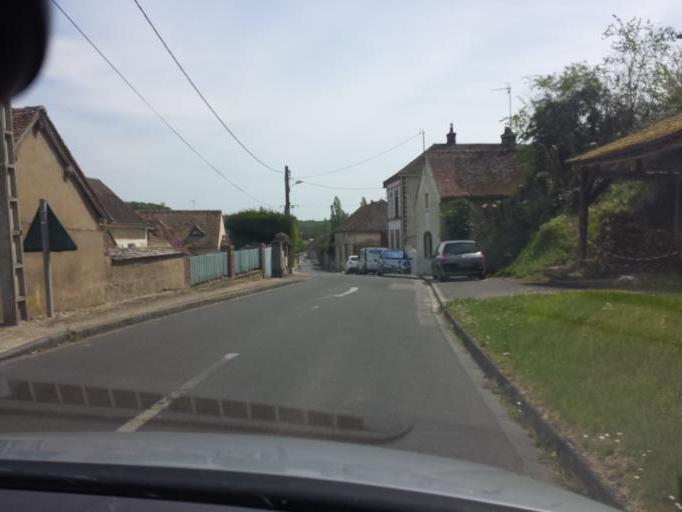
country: FR
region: Centre
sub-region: Departement d'Eure-et-Loir
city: Anet
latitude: 48.8481
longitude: 1.4573
